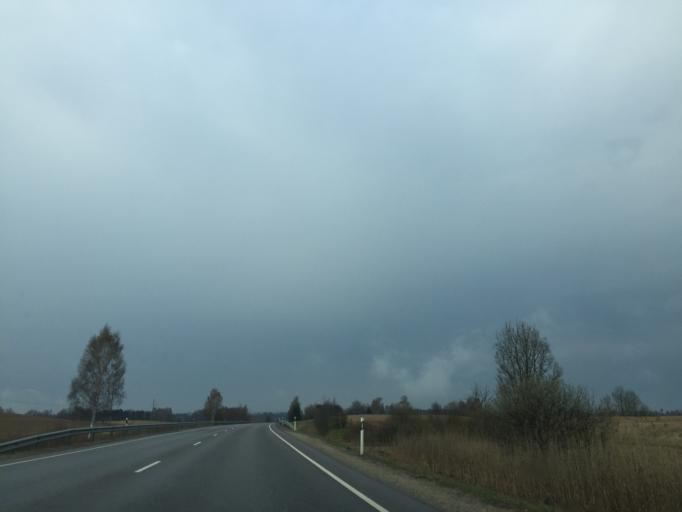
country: EE
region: Tartu
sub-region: UElenurme vald
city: Ulenurme
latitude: 58.1556
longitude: 26.6937
